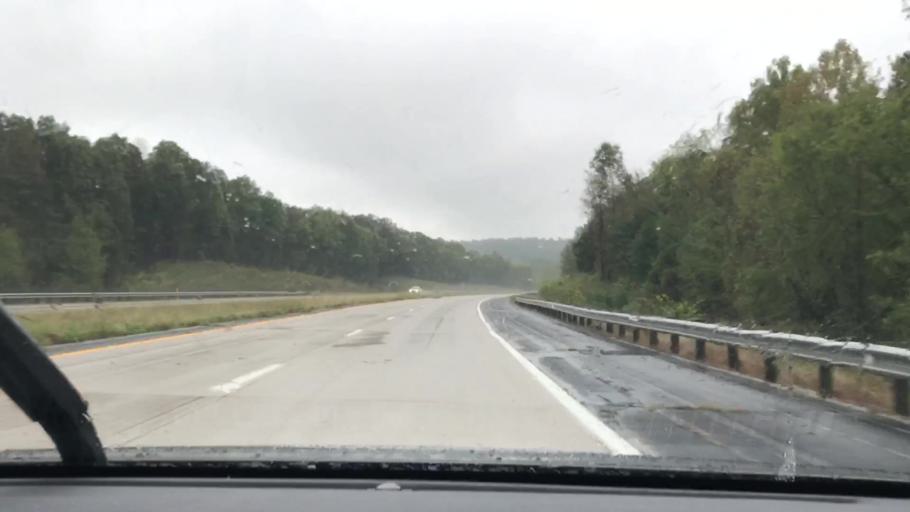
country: US
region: Kentucky
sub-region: Hopkins County
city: Nortonville
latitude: 37.1335
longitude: -87.4578
